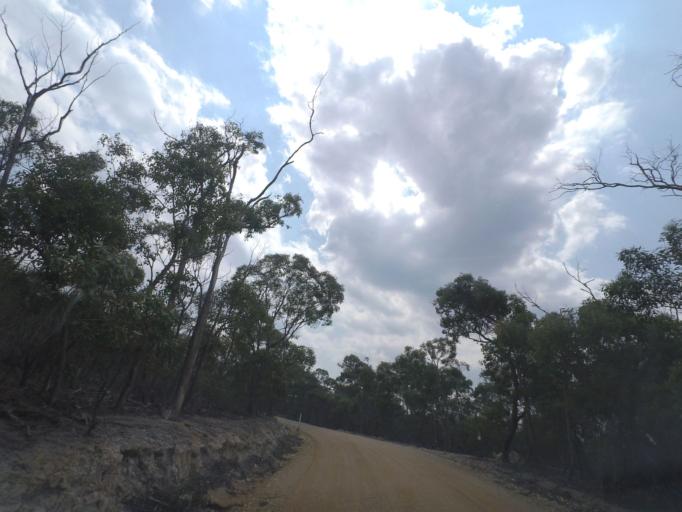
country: AU
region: Victoria
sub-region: Moorabool
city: Bacchus Marsh
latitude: -37.6083
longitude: 144.4436
